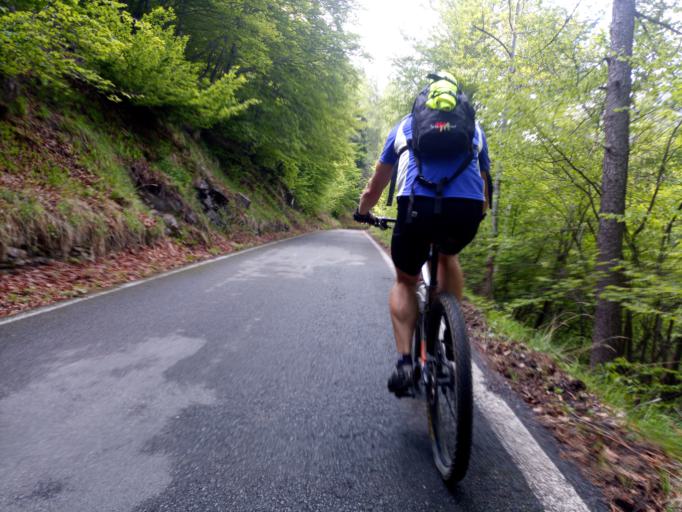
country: IT
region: Piedmont
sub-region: Provincia di Torino
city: Meana di Susa
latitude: 45.1041
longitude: 7.0653
